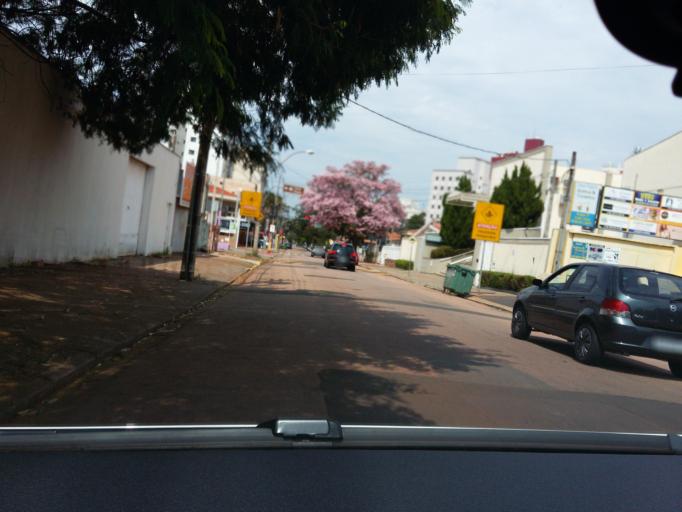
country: BR
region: Sao Paulo
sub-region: Campinas
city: Campinas
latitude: -22.8824
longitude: -47.0687
